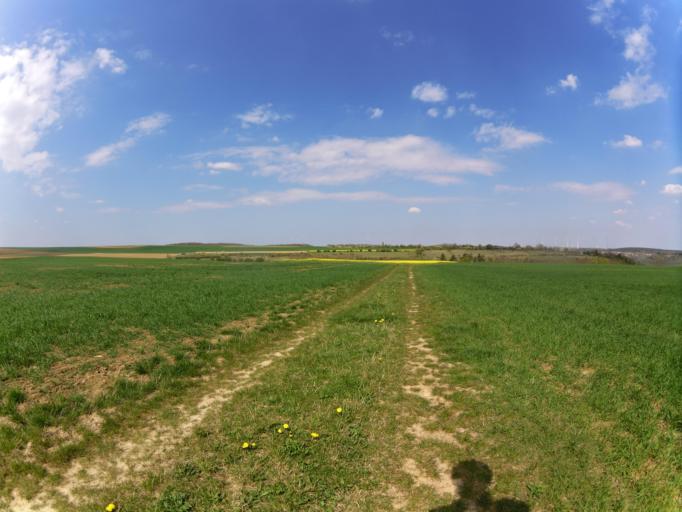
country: DE
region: Bavaria
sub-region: Regierungsbezirk Unterfranken
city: Winterhausen
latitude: 49.6835
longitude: 10.0127
